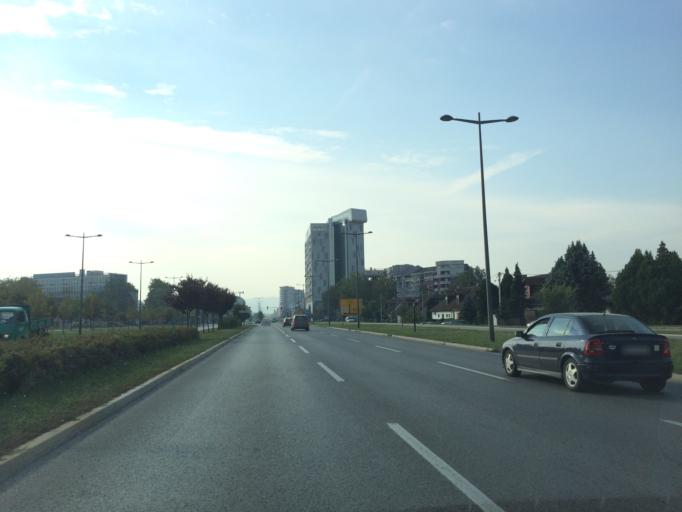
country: RS
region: Autonomna Pokrajina Vojvodina
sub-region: Juznobacki Okrug
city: Novi Sad
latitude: 45.2506
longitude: 19.8152
